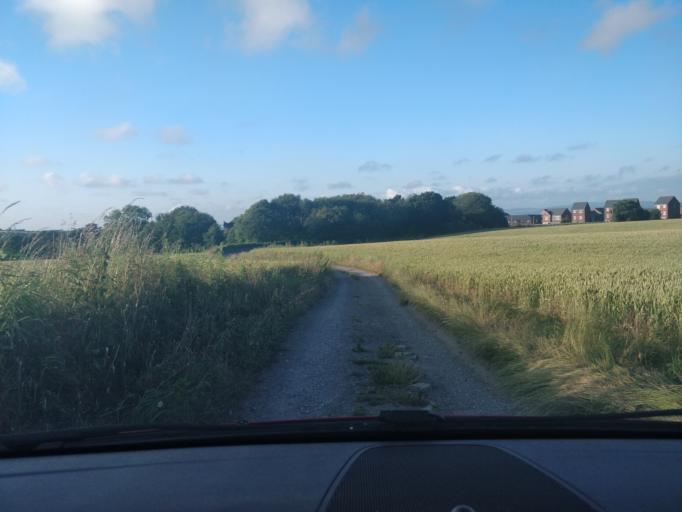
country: GB
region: England
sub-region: St. Helens
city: Billinge
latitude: 53.5182
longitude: -2.7270
